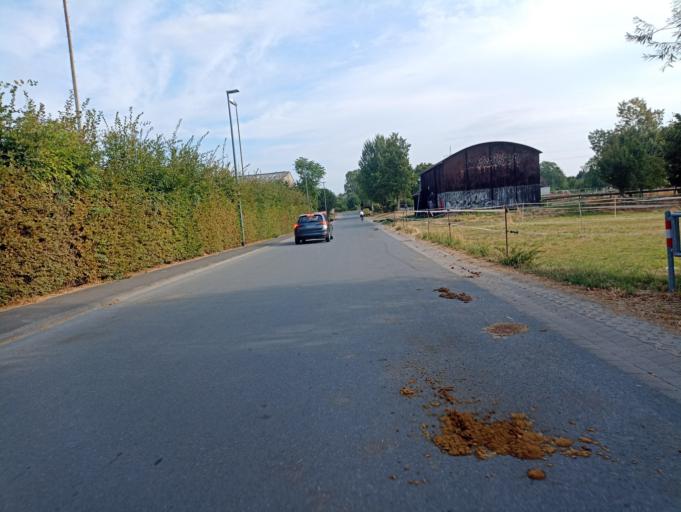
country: DE
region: Hesse
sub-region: Regierungsbezirk Darmstadt
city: Oberursel
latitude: 50.1984
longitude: 8.6049
